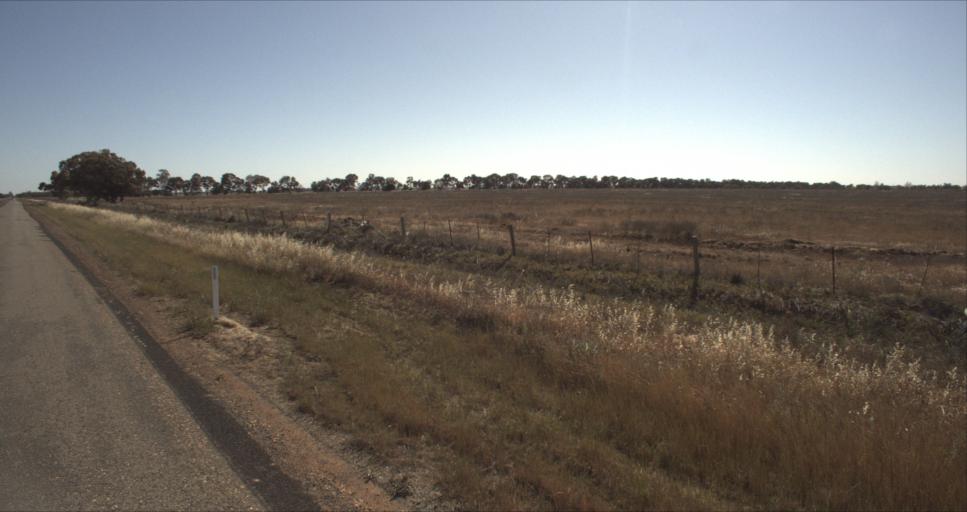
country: AU
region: New South Wales
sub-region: Leeton
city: Leeton
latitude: -34.5813
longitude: 146.2615
